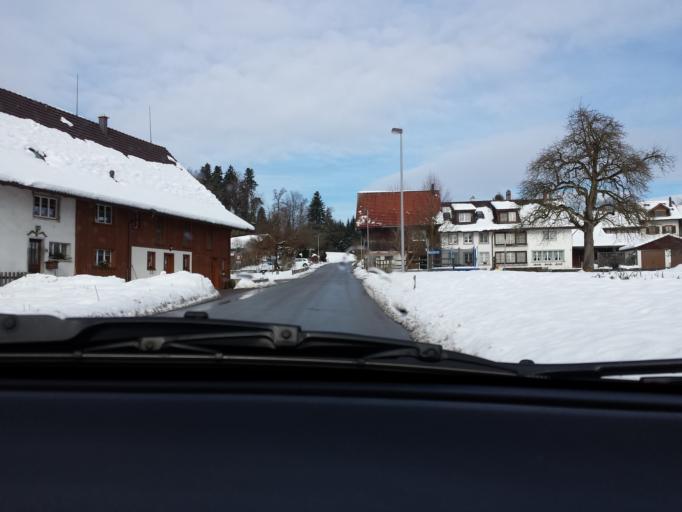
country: CH
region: Zurich
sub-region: Bezirk Hinwil
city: Wetzikon / Unter-Wetzikon
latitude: 47.2976
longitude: 8.7972
